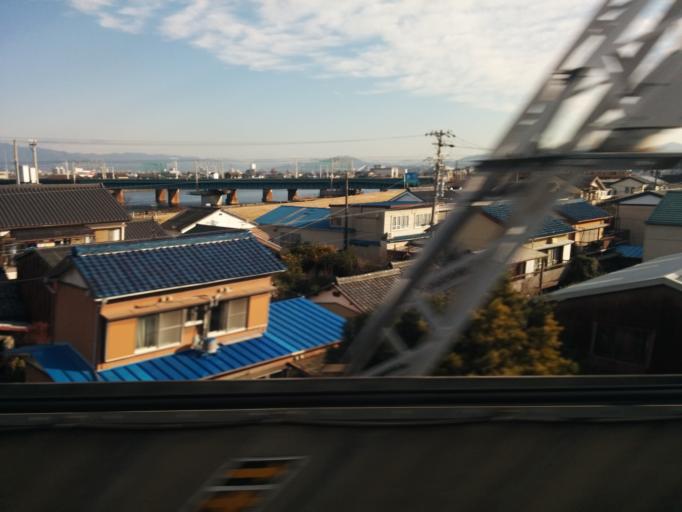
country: JP
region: Aichi
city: Toyohashi
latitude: 34.7772
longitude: 137.3704
